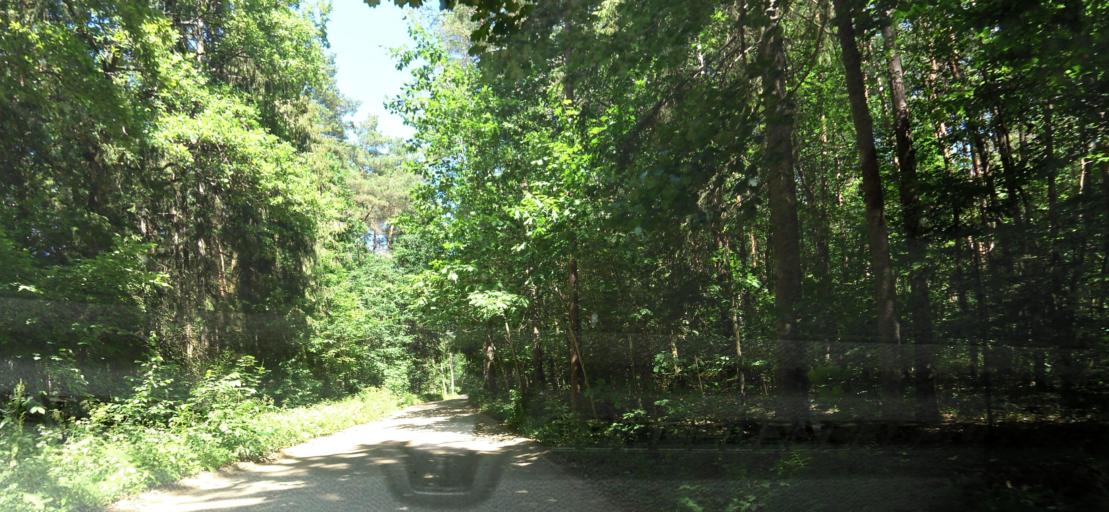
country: LT
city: Grigiskes
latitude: 54.8009
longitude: 24.9845
